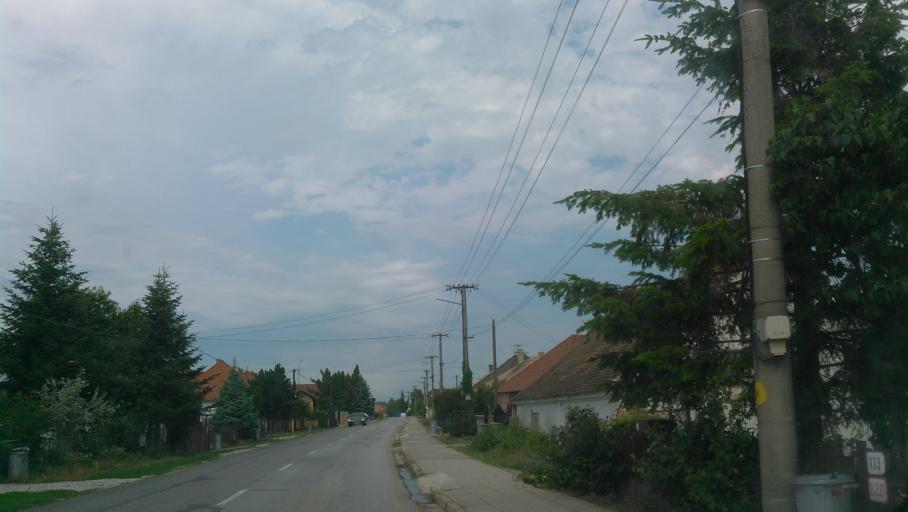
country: SK
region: Trnavsky
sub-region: Okres Trnava
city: Piestany
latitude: 48.4951
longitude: 17.9743
